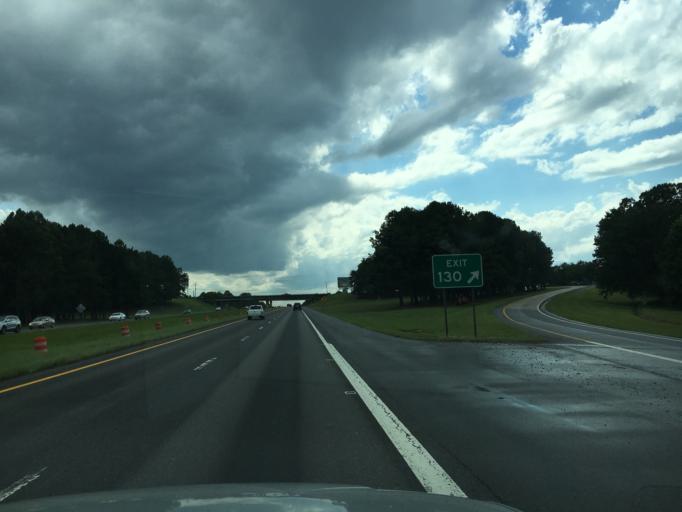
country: US
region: North Carolina
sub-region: Catawba County
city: Conover
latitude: 35.7158
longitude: -81.2252
